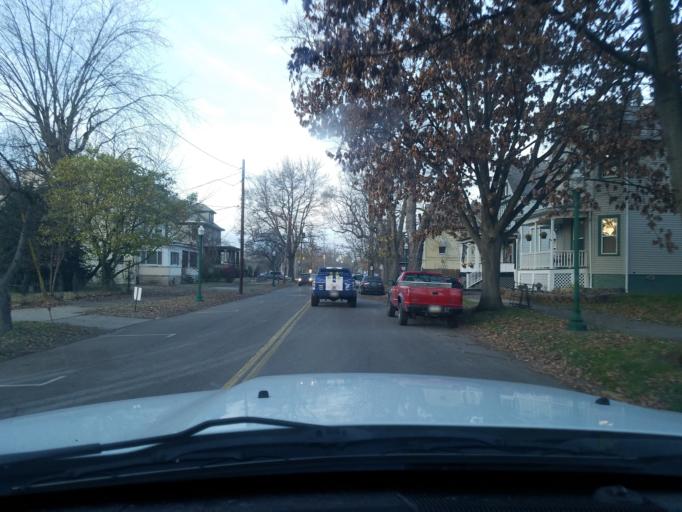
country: US
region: Ohio
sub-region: Washington County
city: Marietta
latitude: 39.4121
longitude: -81.4596
